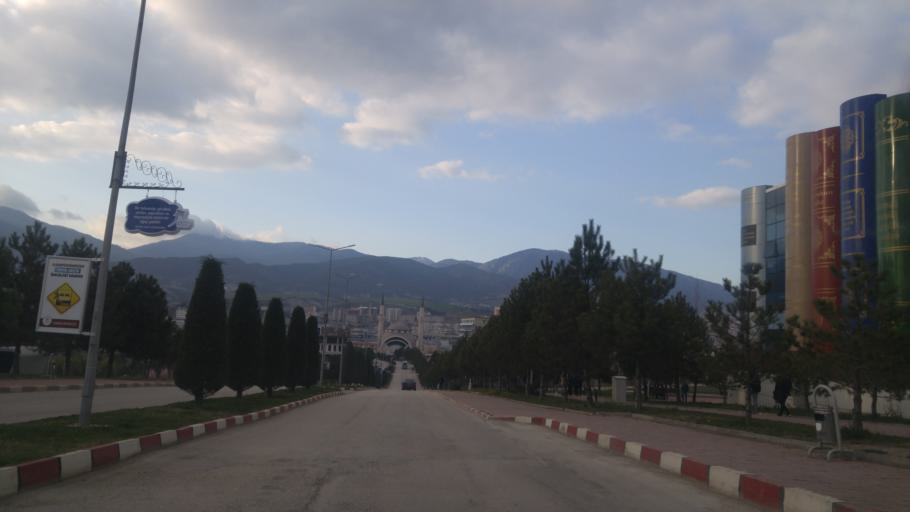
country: TR
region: Karabuk
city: Karabuk
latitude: 41.2078
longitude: 32.6573
